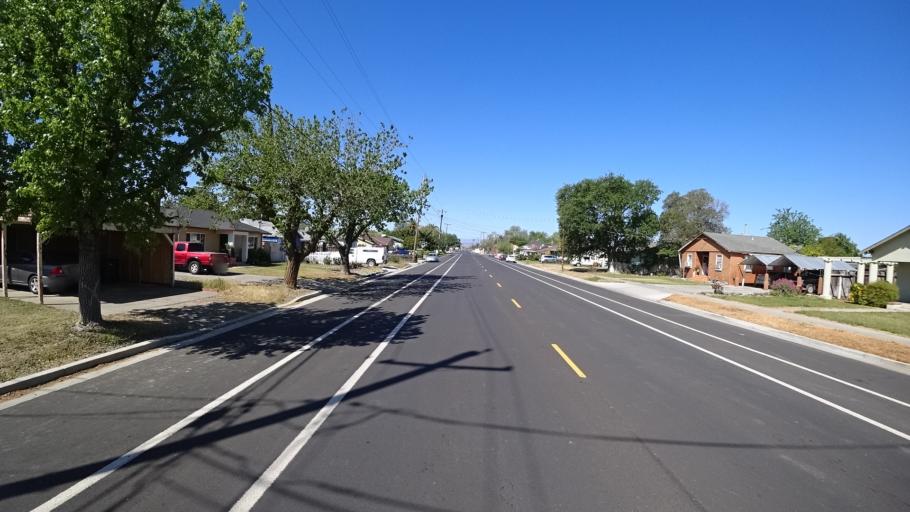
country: US
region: California
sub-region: Glenn County
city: Orland
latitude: 39.7495
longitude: -122.1857
